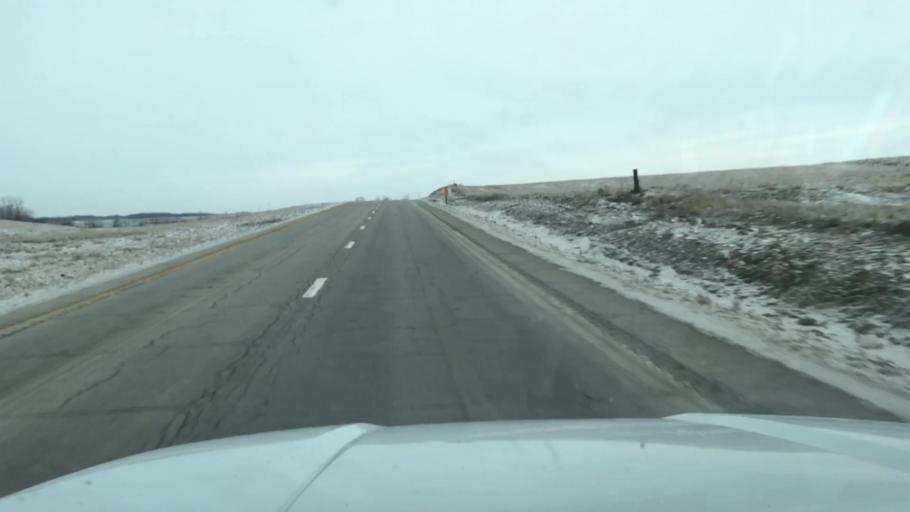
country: US
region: Missouri
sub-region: Andrew County
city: Savannah
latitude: 39.9754
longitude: -94.8757
